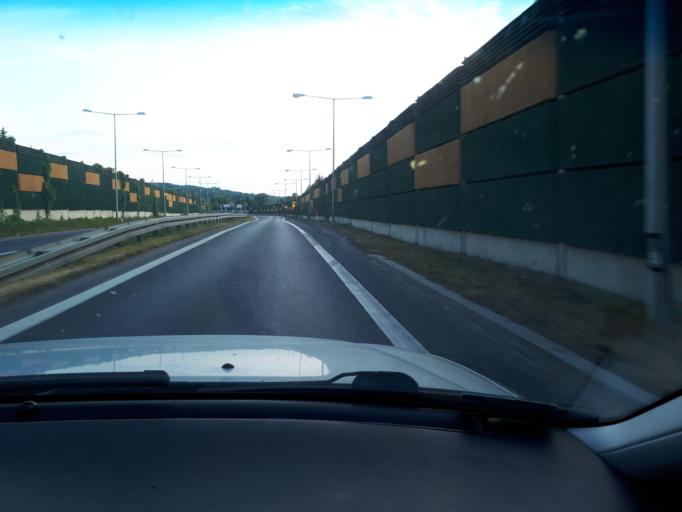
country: PL
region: Subcarpathian Voivodeship
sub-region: Powiat ropczycko-sedziszowski
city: Ropczyce
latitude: 50.0591
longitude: 21.6350
